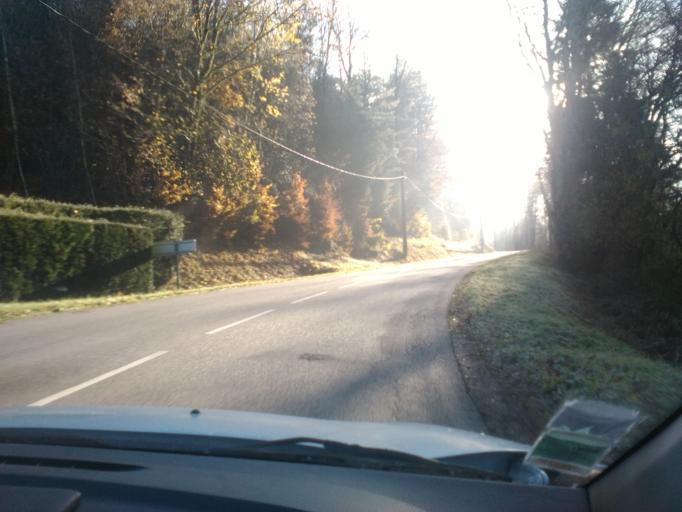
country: FR
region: Lorraine
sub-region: Departement des Vosges
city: Uzemain
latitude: 48.0695
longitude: 6.3151
